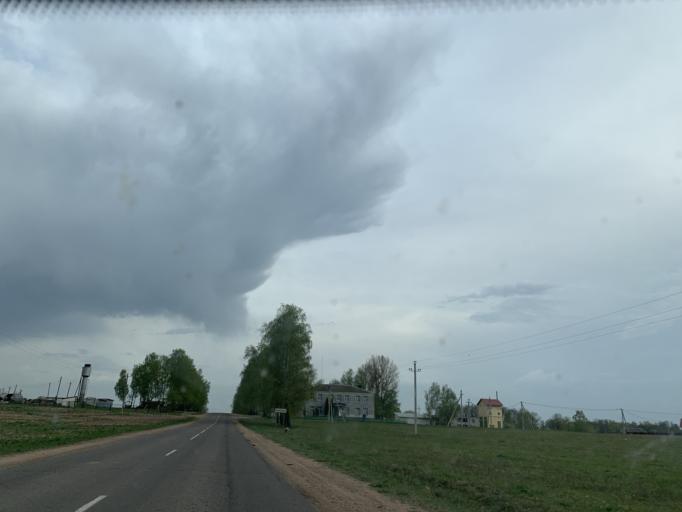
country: BY
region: Minsk
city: Kapyl'
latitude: 53.2652
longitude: 26.9572
